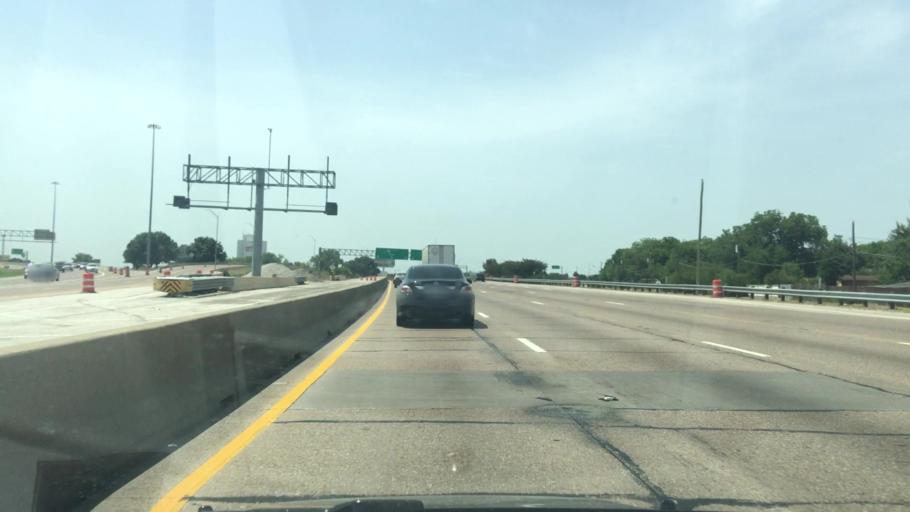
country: US
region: Texas
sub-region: Dallas County
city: Cockrell Hill
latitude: 32.7111
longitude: -96.8303
